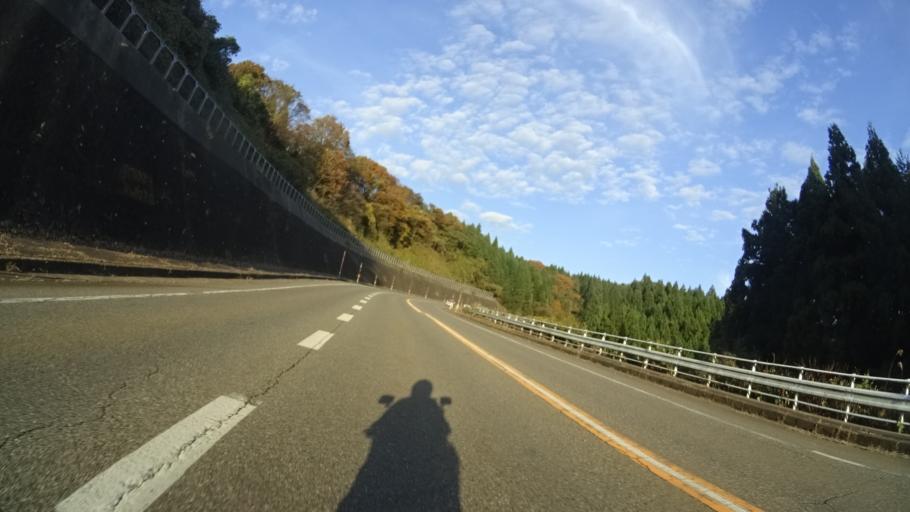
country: JP
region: Niigata
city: Kashiwazaki
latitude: 37.4067
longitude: 138.6447
